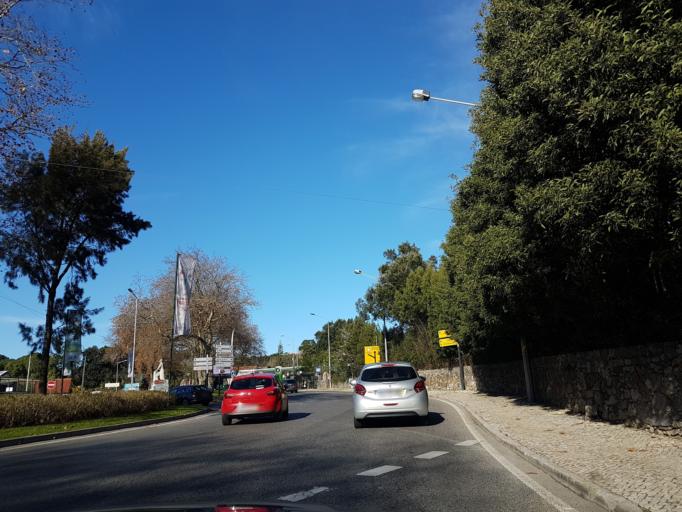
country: PT
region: Lisbon
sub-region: Sintra
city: Sintra
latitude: 38.7872
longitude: -9.3729
